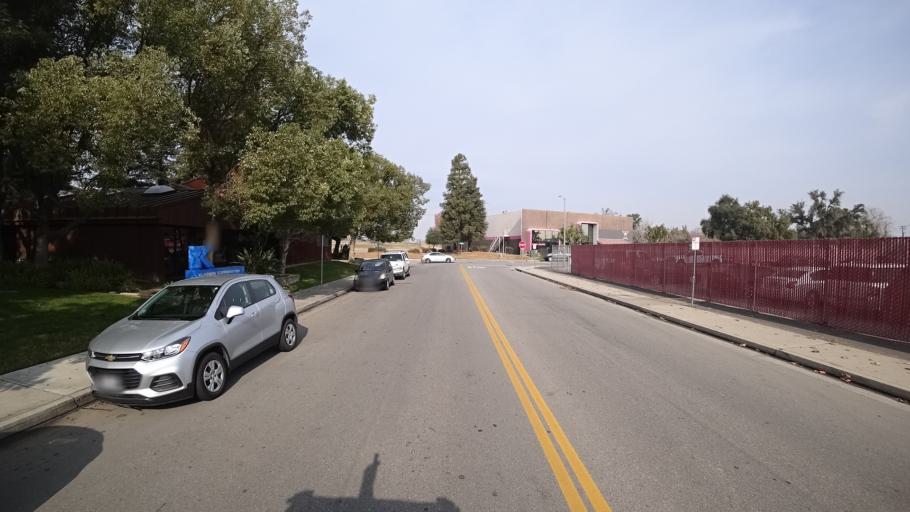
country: US
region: California
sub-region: Kern County
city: Bakersfield
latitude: 35.3777
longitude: -119.0426
